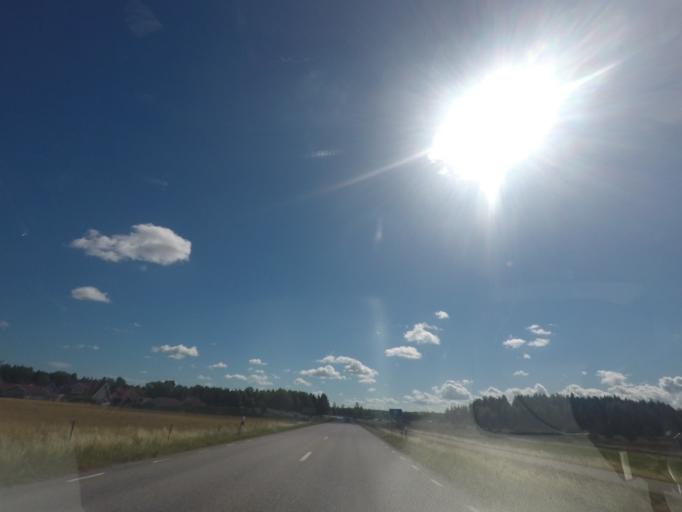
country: SE
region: Uppsala
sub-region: Uppsala Kommun
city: Saevja
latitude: 59.8567
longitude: 17.8184
